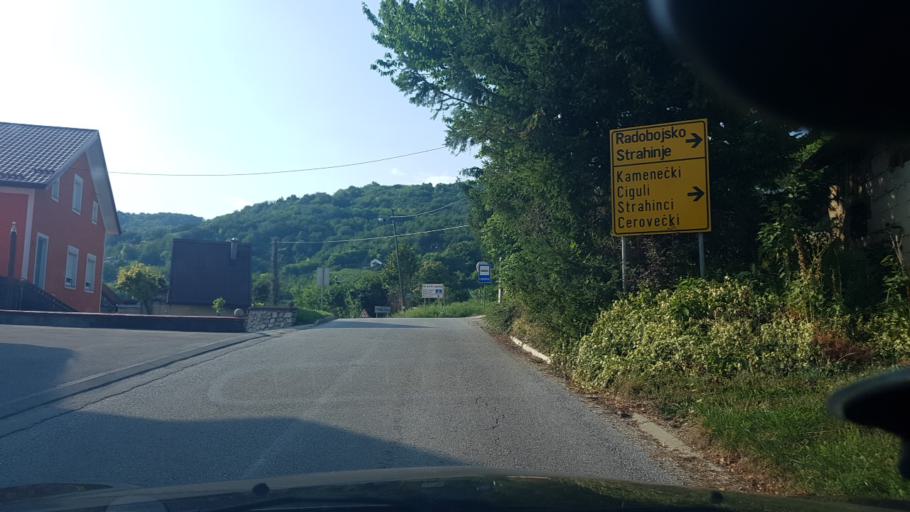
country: HR
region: Krapinsko-Zagorska
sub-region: Grad Krapina
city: Krapina
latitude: 46.1642
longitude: 15.8940
